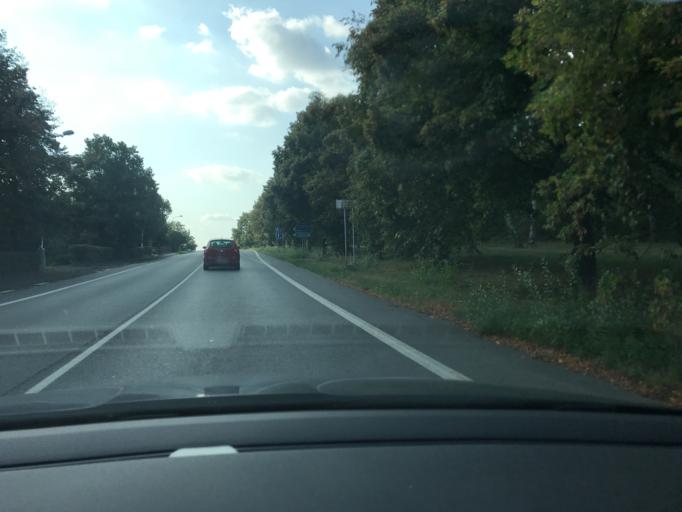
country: CZ
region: Central Bohemia
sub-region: Okres Kladno
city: Slany
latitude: 50.2347
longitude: 14.0767
